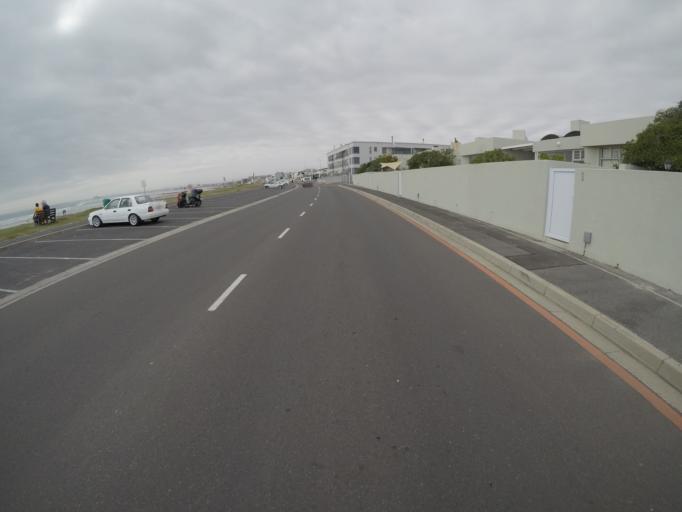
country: ZA
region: Western Cape
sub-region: City of Cape Town
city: Sunset Beach
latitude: -33.7259
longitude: 18.4424
